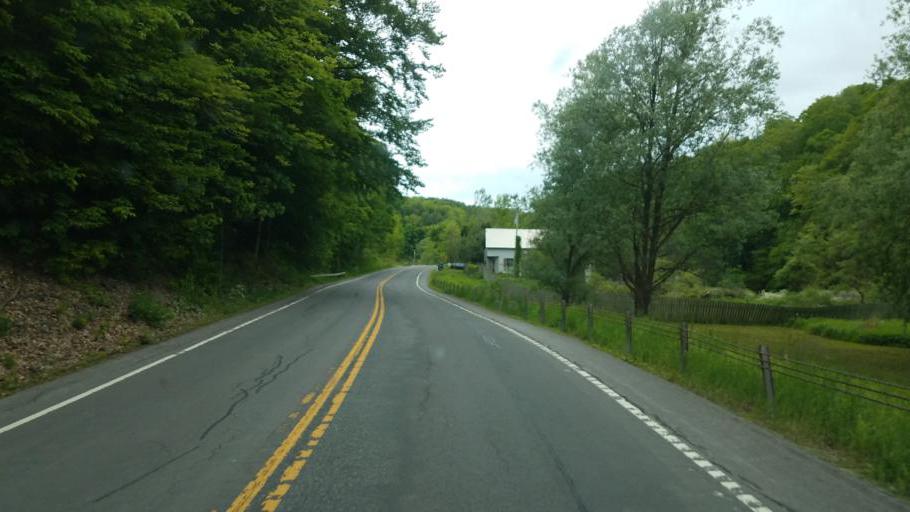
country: US
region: New York
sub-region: Herkimer County
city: Frankfort
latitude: 42.9687
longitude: -75.1009
